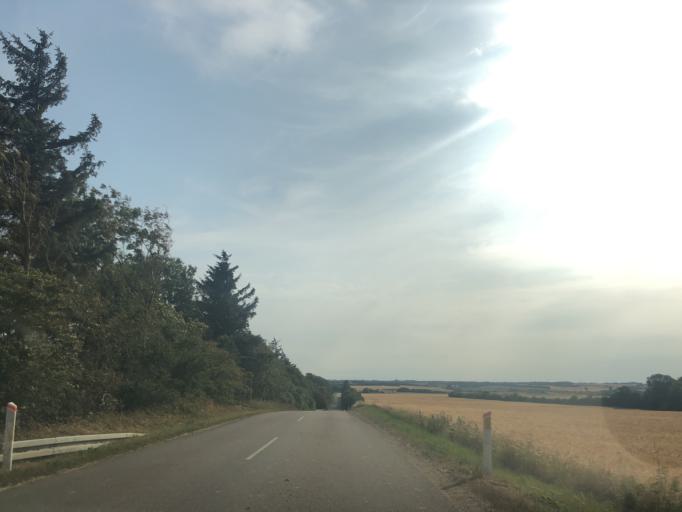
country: DK
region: Central Jutland
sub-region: Skive Kommune
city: Skive
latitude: 56.7496
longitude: 9.0451
